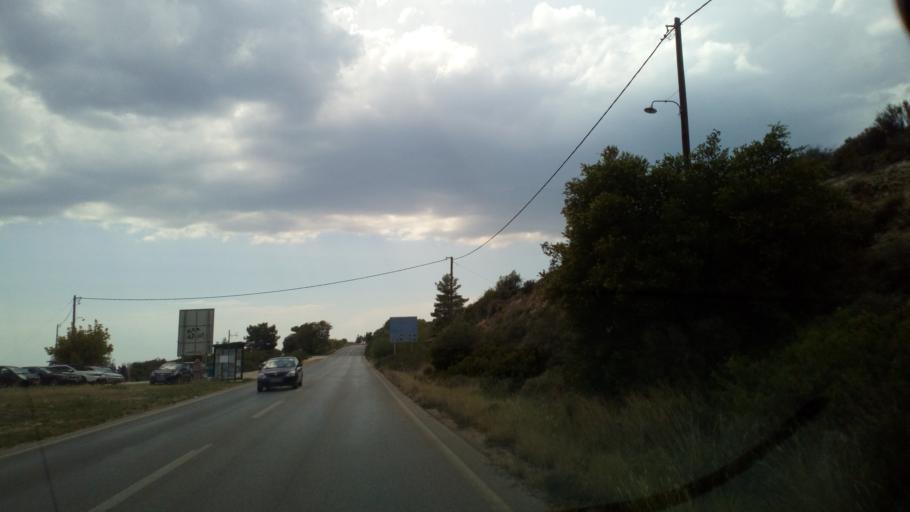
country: GR
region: Central Macedonia
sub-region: Nomos Chalkidikis
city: Ormylia
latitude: 40.2605
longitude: 23.4802
